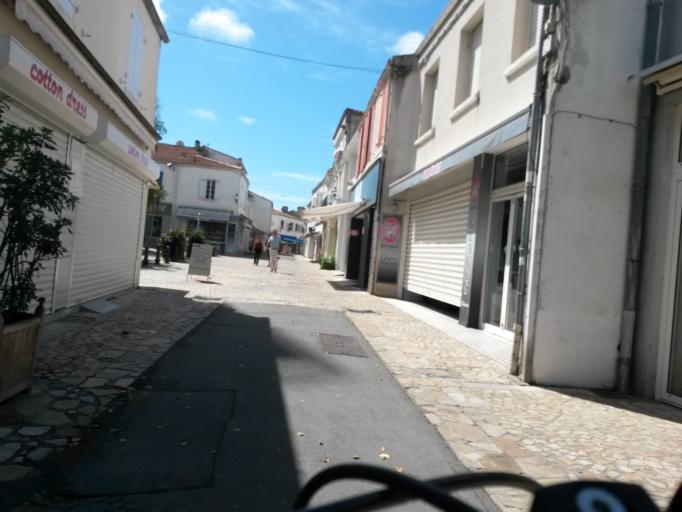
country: FR
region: Poitou-Charentes
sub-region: Departement de la Charente-Maritime
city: Dolus-d'Oleron
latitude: 45.9441
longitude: -1.3057
